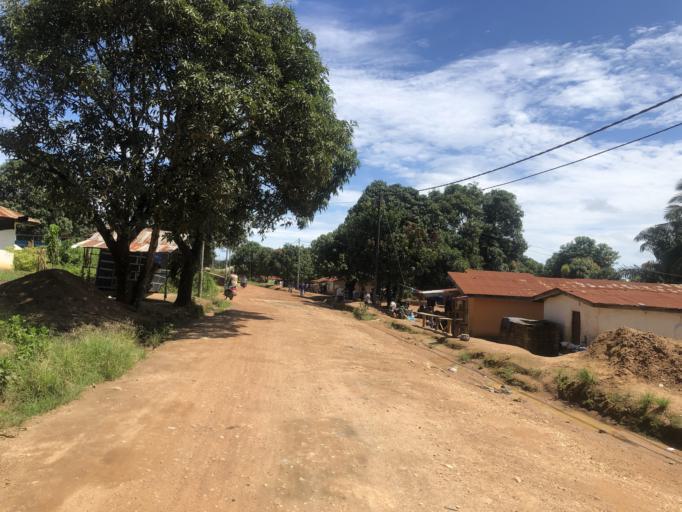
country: SL
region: Eastern Province
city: Koidu
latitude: 8.6399
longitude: -10.9552
